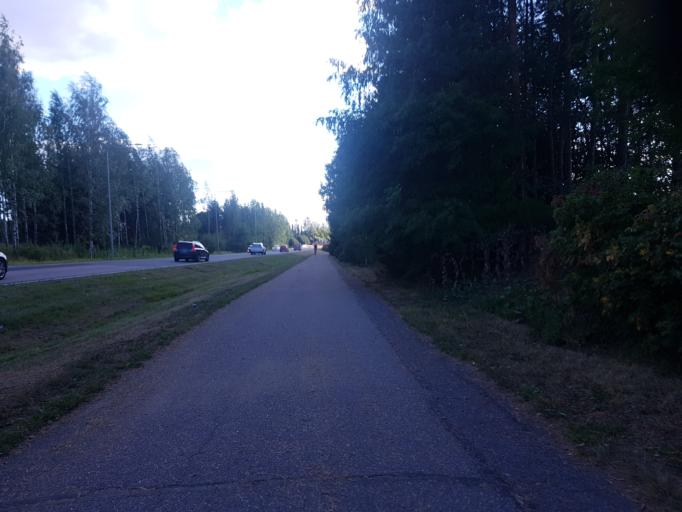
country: FI
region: Uusimaa
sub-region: Helsinki
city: Vantaa
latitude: 60.2775
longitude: 25.0048
